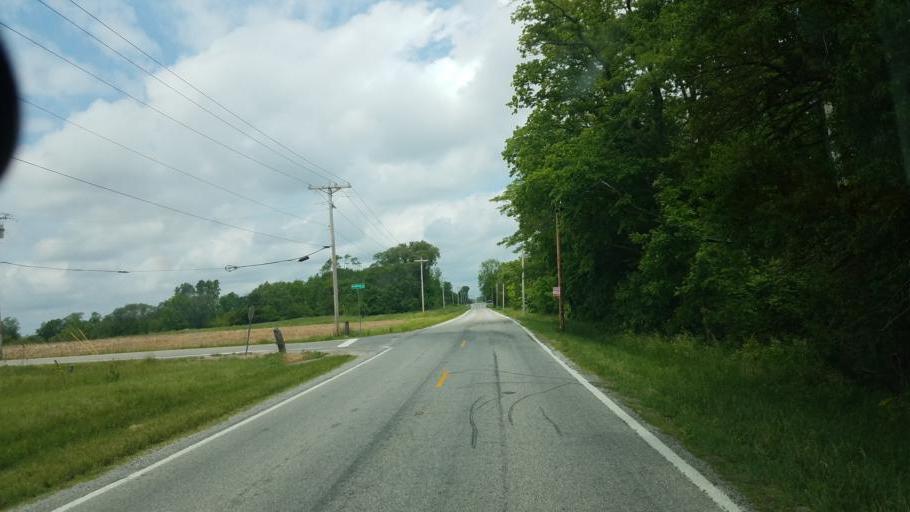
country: US
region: Ohio
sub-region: Marion County
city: Prospect
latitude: 40.4164
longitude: -83.1983
